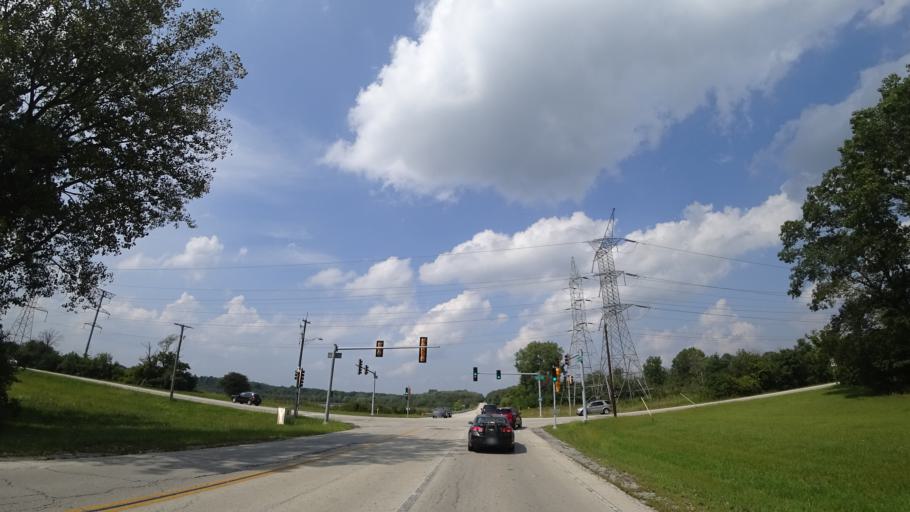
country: US
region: Illinois
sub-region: Will County
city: Goodings Grove
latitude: 41.6508
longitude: -87.9121
